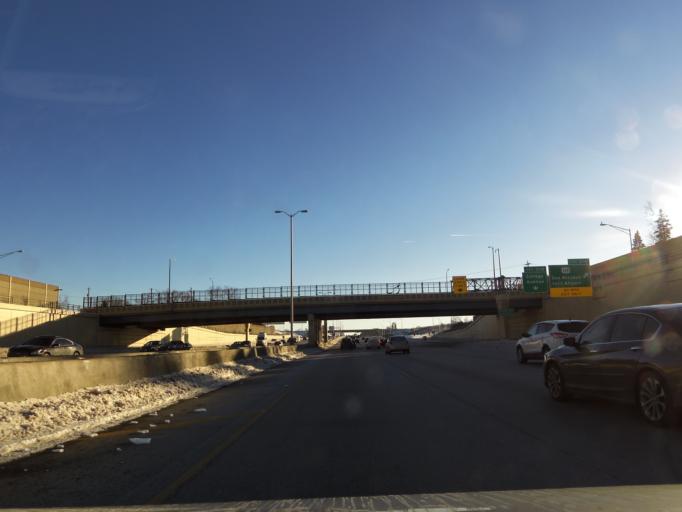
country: US
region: Wisconsin
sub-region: Milwaukee County
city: Greendale
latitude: 42.9459
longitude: -87.9351
